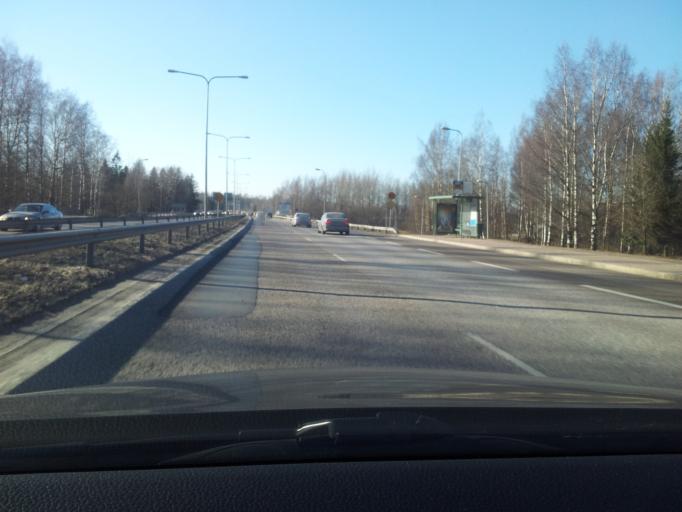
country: FI
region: Uusimaa
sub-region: Helsinki
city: Vantaa
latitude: 60.2411
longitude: 25.0314
